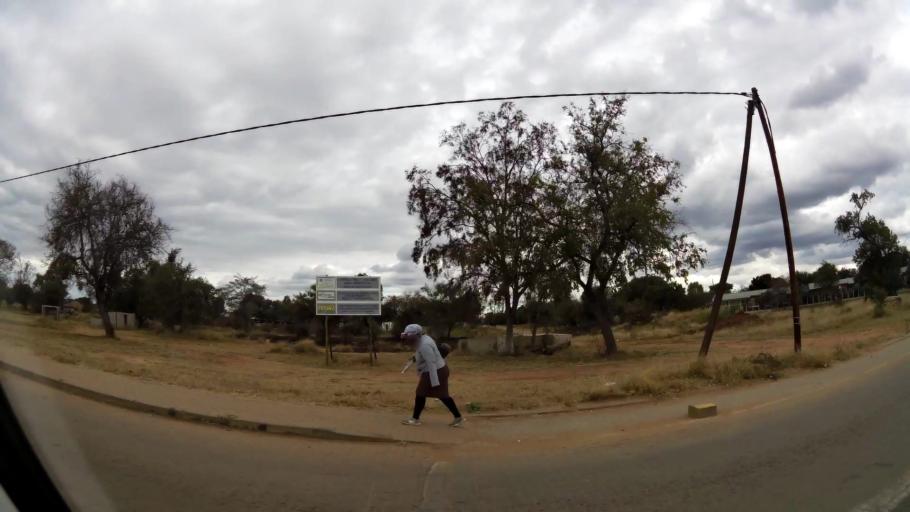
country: ZA
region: Limpopo
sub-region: Waterberg District Municipality
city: Modimolle
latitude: -24.7022
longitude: 28.4135
